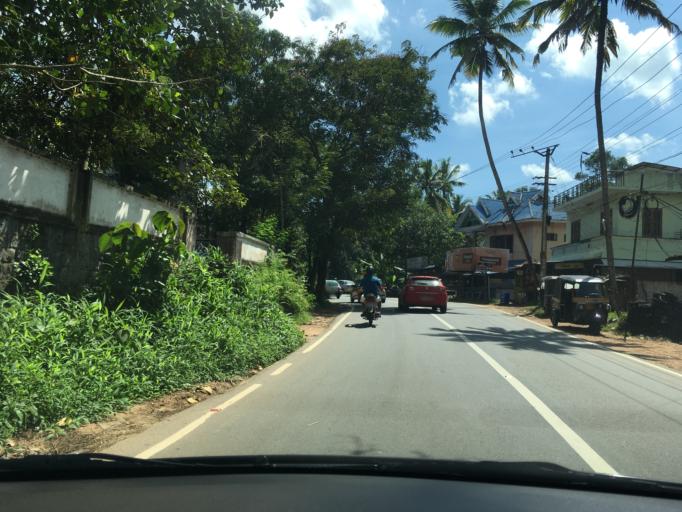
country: IN
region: Kerala
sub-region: Thiruvananthapuram
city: Nedumangad
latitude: 8.5879
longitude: 76.9955
